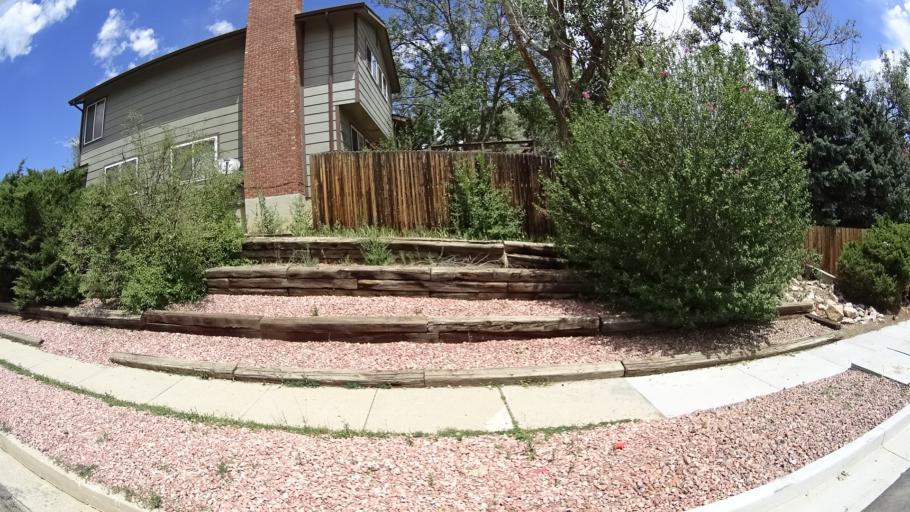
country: US
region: Colorado
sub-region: El Paso County
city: Stratmoor
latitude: 38.7863
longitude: -104.8158
